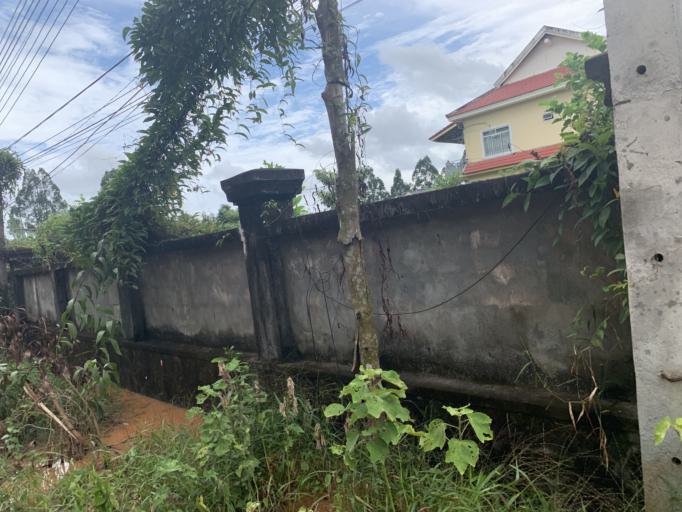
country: KH
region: Koh Kong
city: Koh Kong
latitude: 11.6212
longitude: 102.9819
